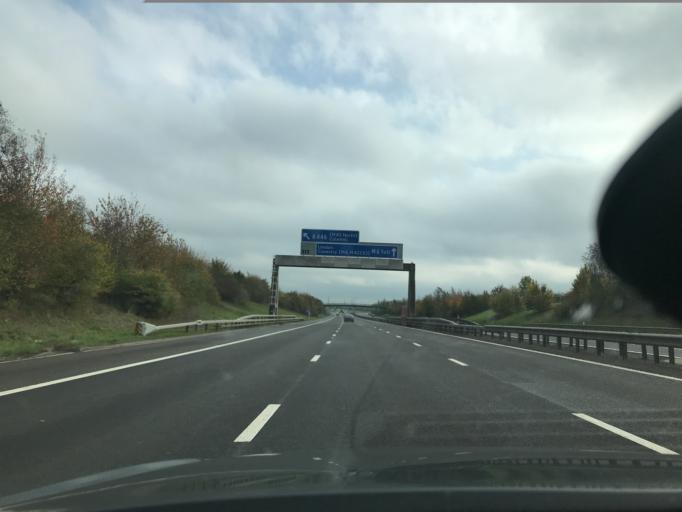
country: GB
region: England
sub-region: Warwickshire
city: Curdworth
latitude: 52.5545
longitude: -1.7431
